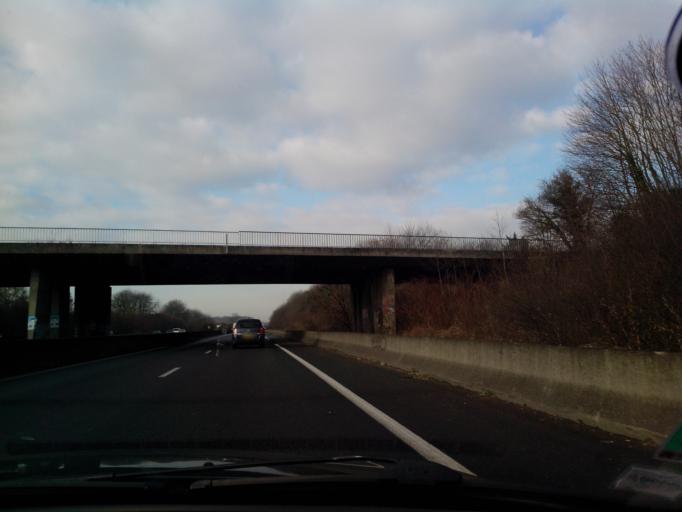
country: FR
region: Ile-de-France
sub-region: Departement du Val-d'Oise
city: Le Plessis-Bouchard
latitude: 49.0099
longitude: 2.2326
